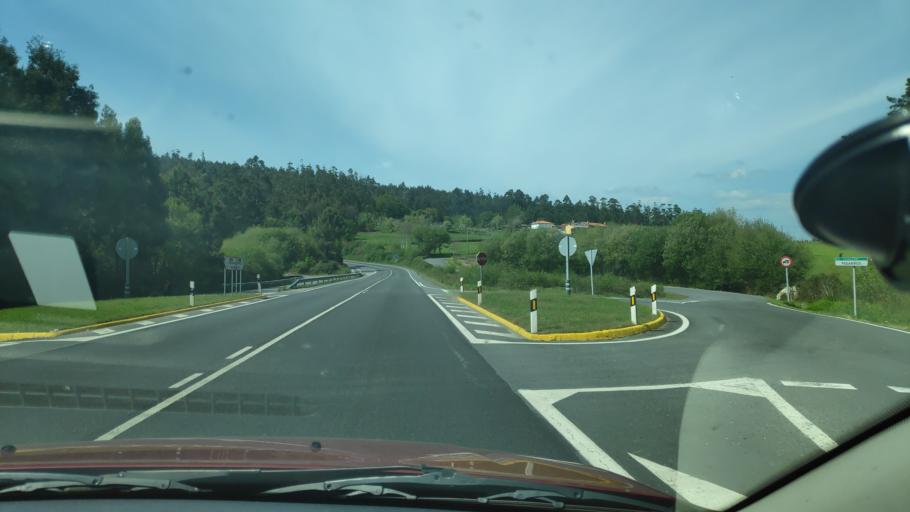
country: ES
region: Galicia
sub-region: Provincia da Coruna
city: Ames
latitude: 42.8774
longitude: -8.6624
